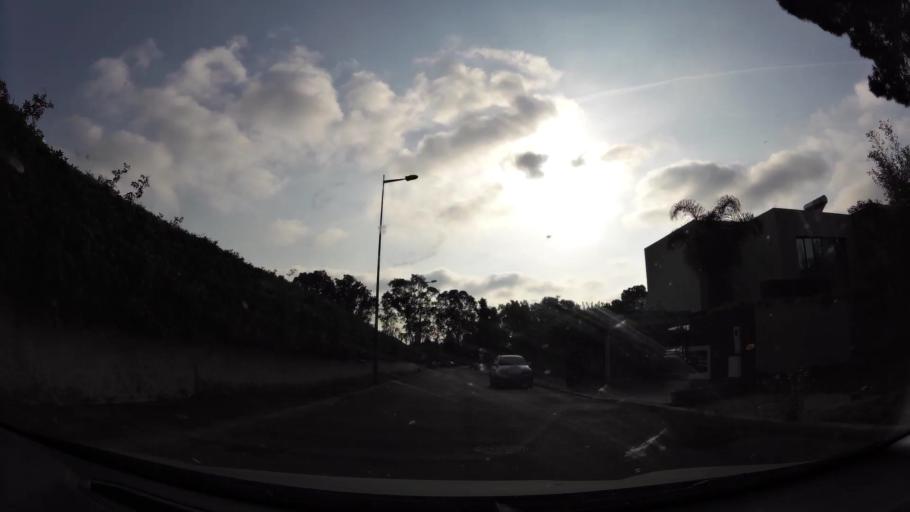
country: MA
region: Rabat-Sale-Zemmour-Zaer
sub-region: Rabat
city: Rabat
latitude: 33.9419
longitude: -6.8201
